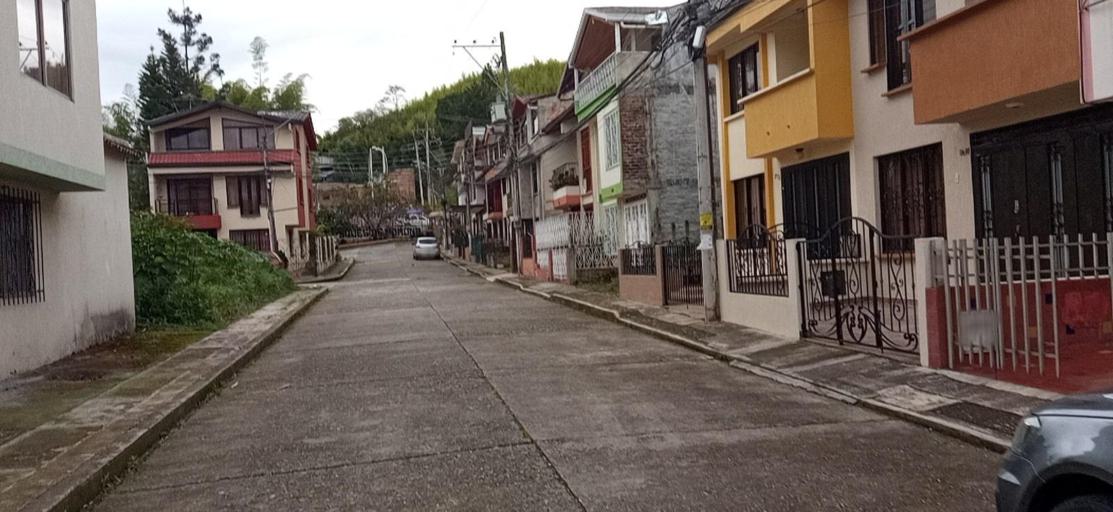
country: CO
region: Cauca
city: Popayan
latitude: 2.4504
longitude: -76.5936
